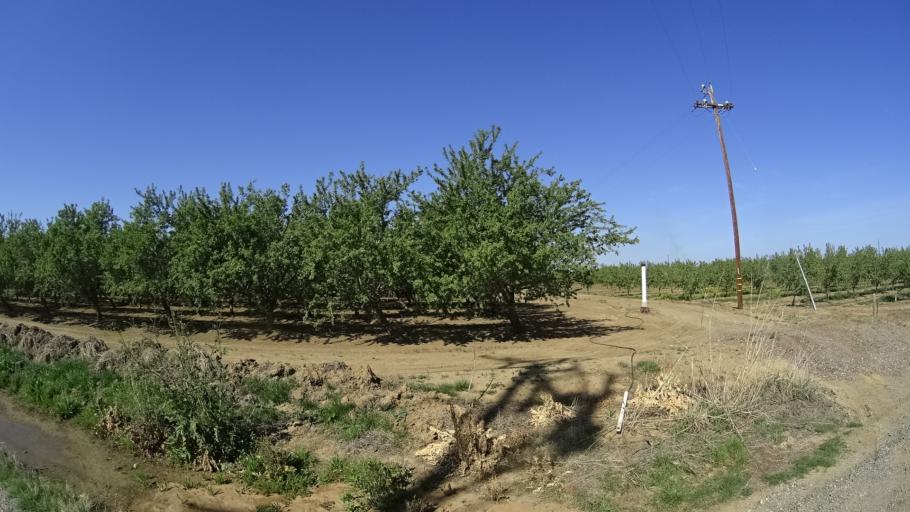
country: US
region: California
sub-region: Glenn County
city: Willows
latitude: 39.5513
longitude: -122.1861
